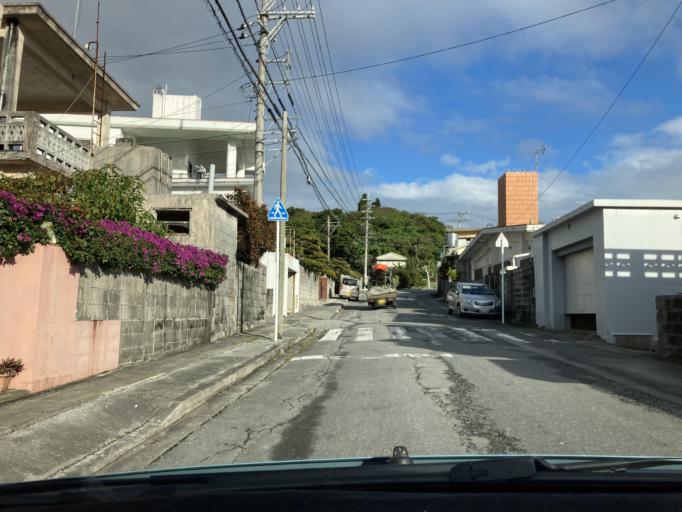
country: JP
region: Okinawa
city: Itoman
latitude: 26.1164
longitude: 127.6730
